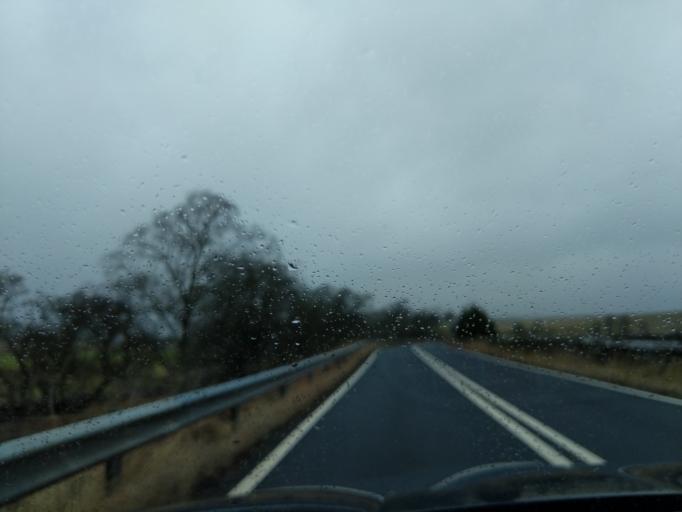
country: GB
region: England
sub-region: Northumberland
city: Rochester
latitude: 55.2457
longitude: -2.2171
